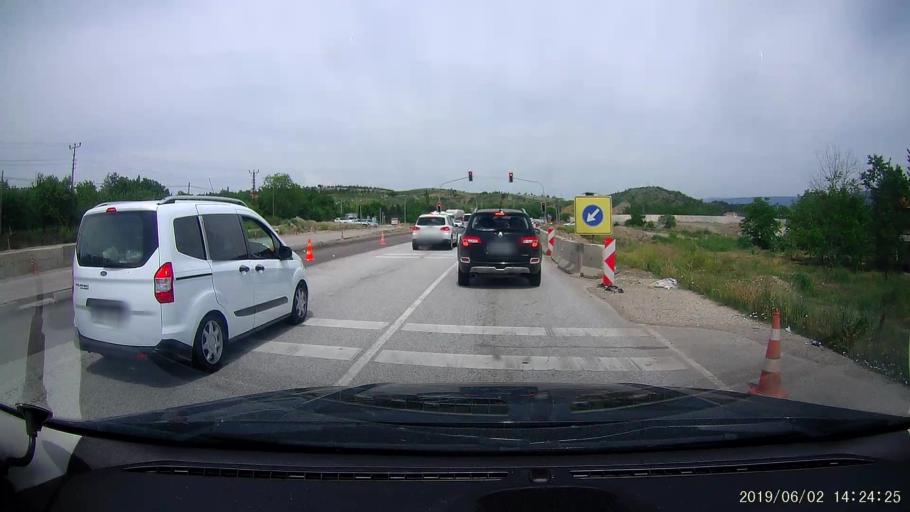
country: TR
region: Kastamonu
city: Tosya
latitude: 41.0013
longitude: 34.0304
